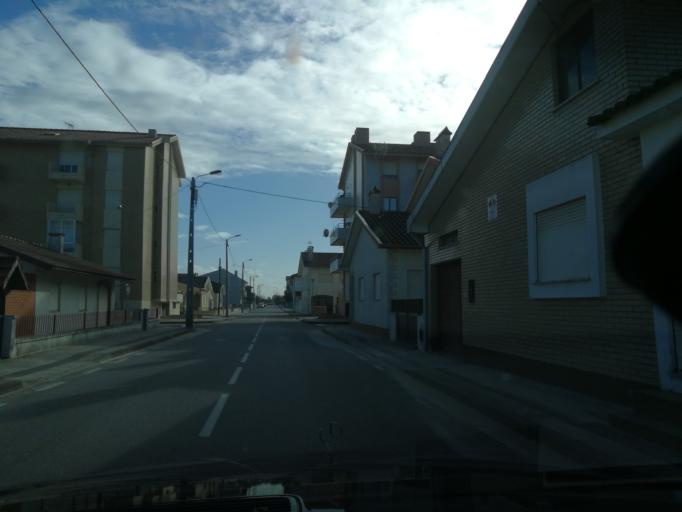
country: PT
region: Aveiro
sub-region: Murtosa
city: Murtosa
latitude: 40.7627
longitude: -8.7086
